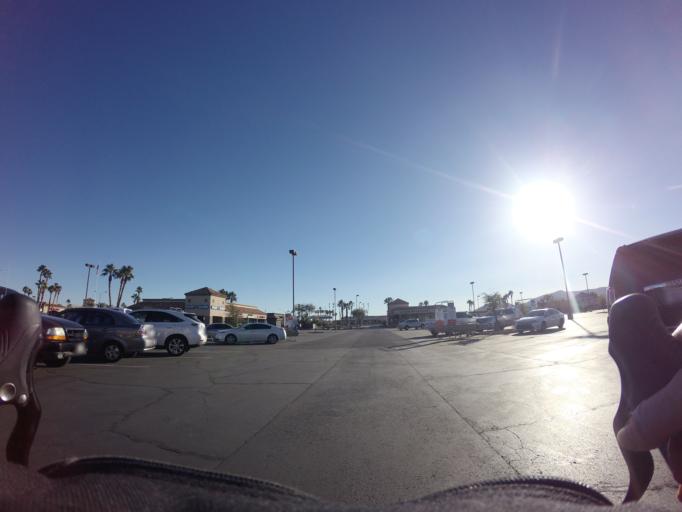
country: US
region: Nevada
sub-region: Clark County
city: Whitney
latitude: 36.0418
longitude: -115.1019
